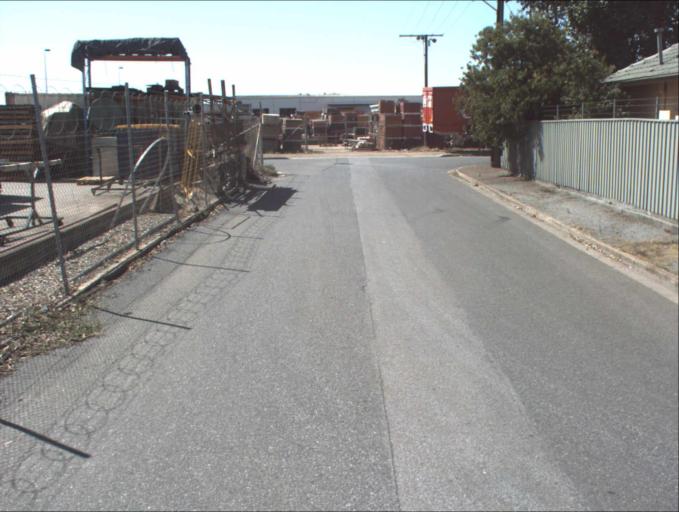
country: AU
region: South Australia
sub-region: Port Adelaide Enfield
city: Alberton
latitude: -34.8410
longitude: 138.5429
